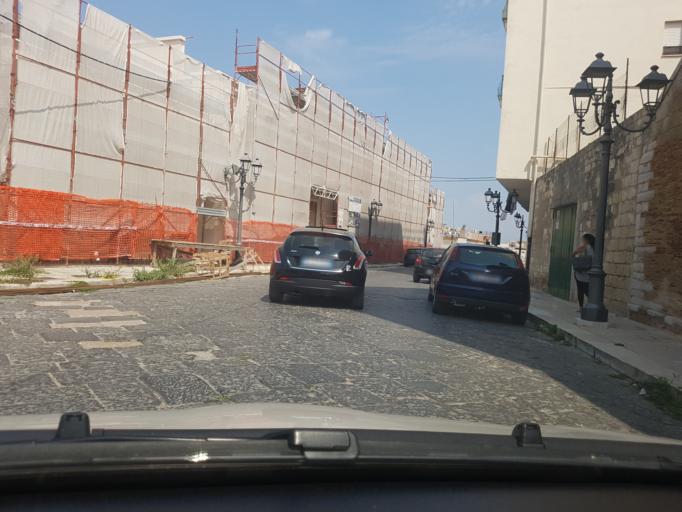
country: IT
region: Apulia
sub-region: Provincia di Foggia
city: Cerignola
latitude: 41.2664
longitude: 15.8924
